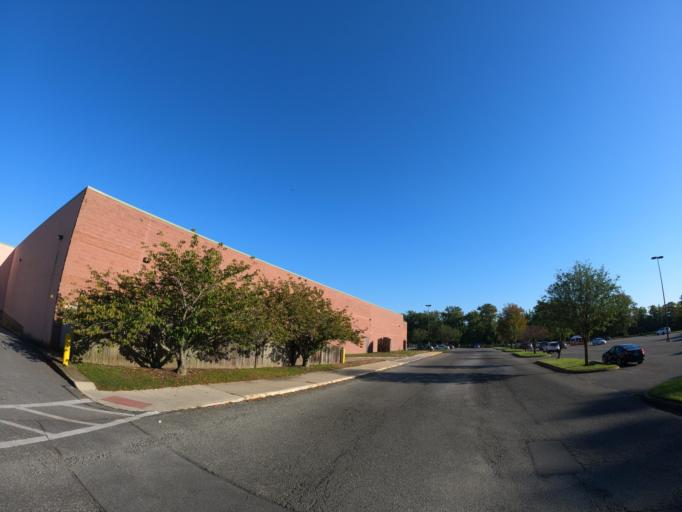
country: US
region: New Jersey
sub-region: Cape May County
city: North Cape May
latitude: 38.9748
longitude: -74.9409
